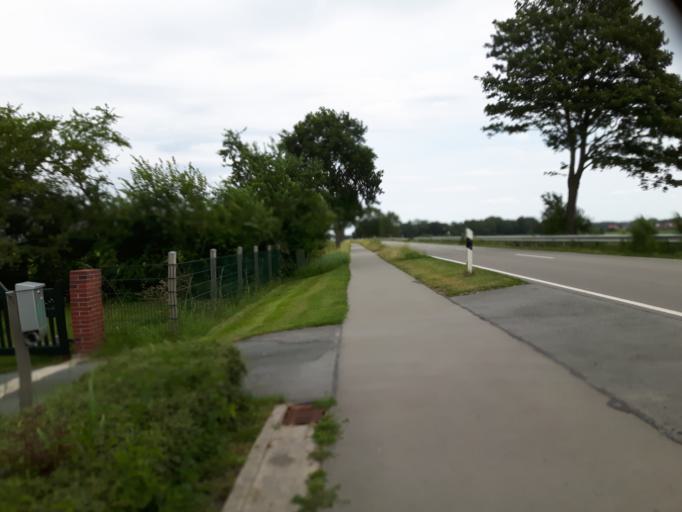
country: DE
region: Lower Saxony
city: Varel
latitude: 53.3897
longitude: 8.2541
